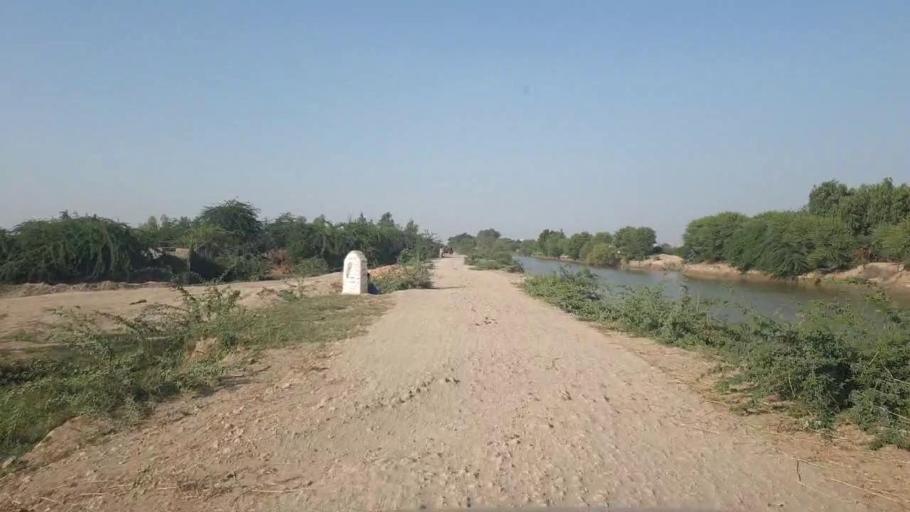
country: PK
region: Sindh
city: Badin
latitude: 24.6491
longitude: 68.8152
